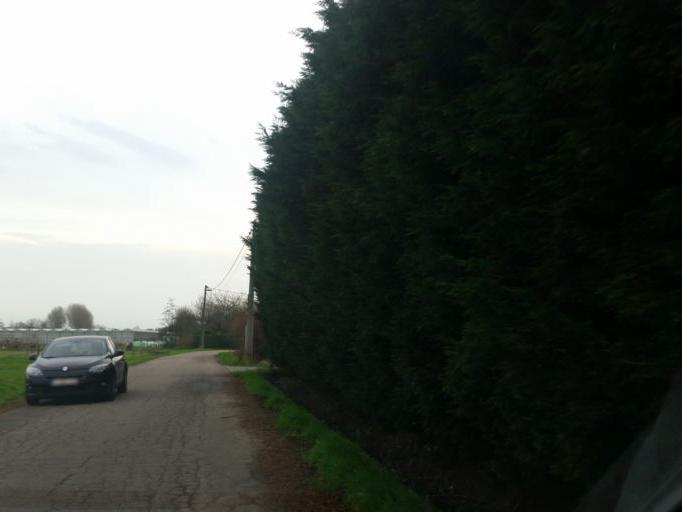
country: BE
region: Flanders
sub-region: Provincie Antwerpen
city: Lier
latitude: 51.1136
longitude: 4.5739
